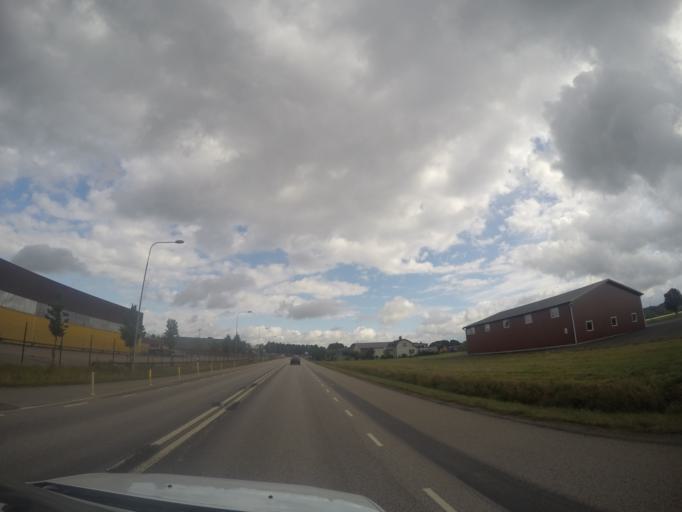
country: SE
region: Kronoberg
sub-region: Ljungby Kommun
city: Ljungby
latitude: 56.8154
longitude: 13.9170
